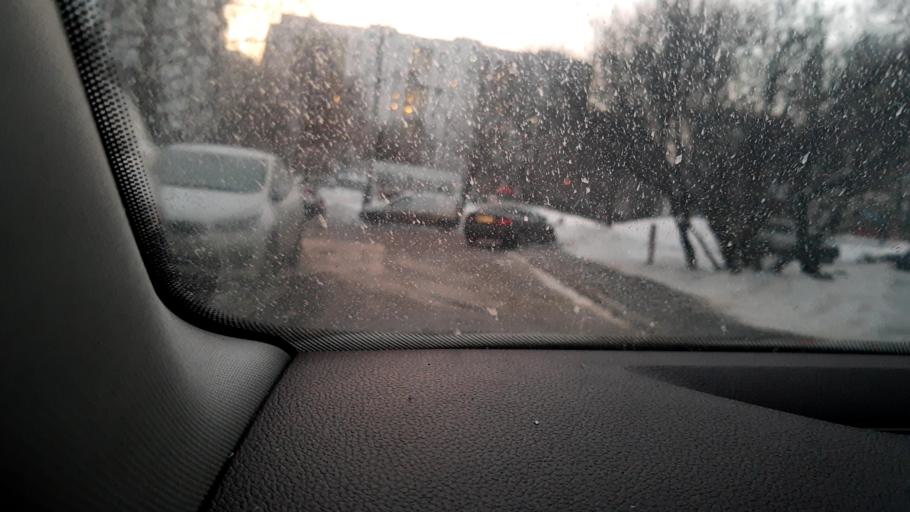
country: RU
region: Moscow
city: Biryulevo
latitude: 55.5842
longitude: 37.6851
